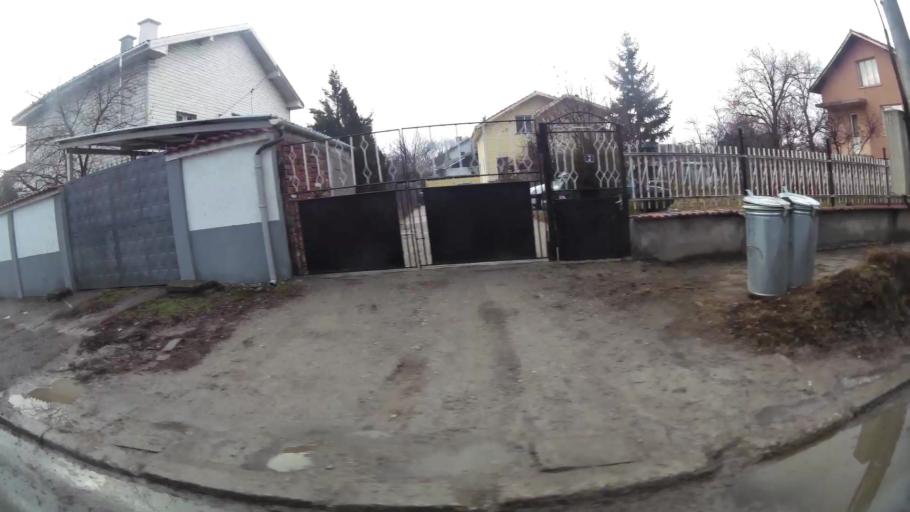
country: BG
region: Sofia-Capital
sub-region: Stolichna Obshtina
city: Sofia
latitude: 42.7363
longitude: 23.3424
